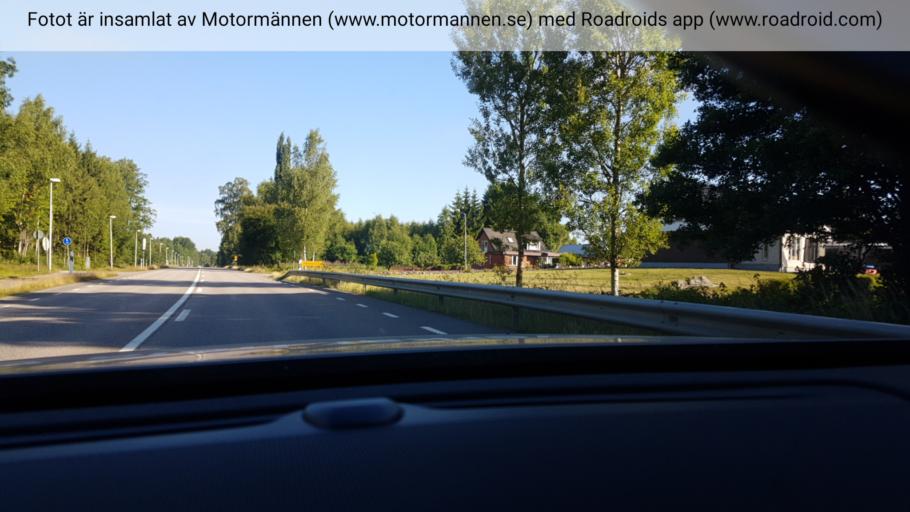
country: SE
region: Skane
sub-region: Hassleholms Kommun
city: Bjarnum
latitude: 56.3090
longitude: 13.6953
